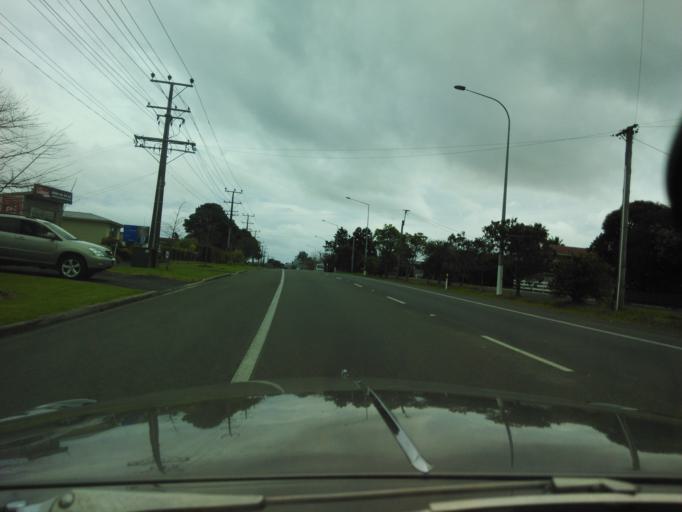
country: NZ
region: Auckland
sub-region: Auckland
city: Muriwai Beach
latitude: -36.7717
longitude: 174.5415
